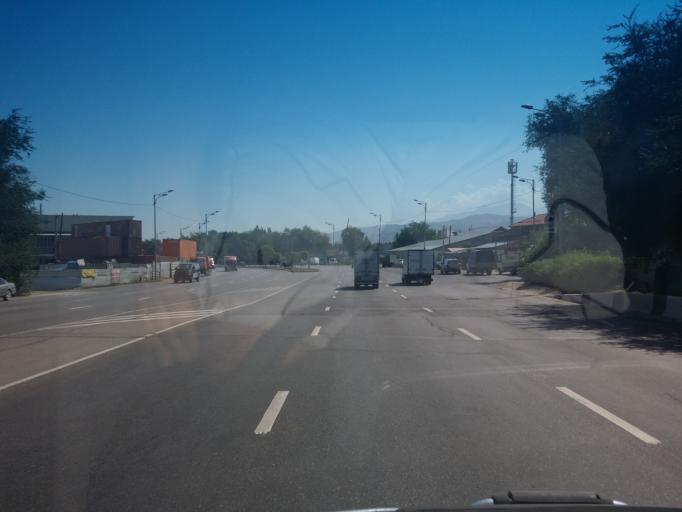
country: KZ
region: Almaty Qalasy
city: Almaty
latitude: 43.2931
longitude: 76.9740
